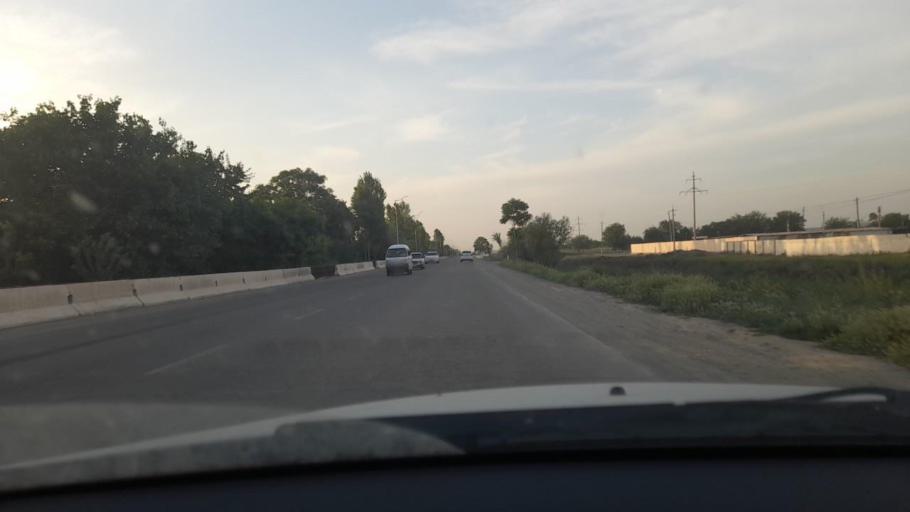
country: UZ
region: Sirdaryo
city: Guliston
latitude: 40.4944
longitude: 68.7359
